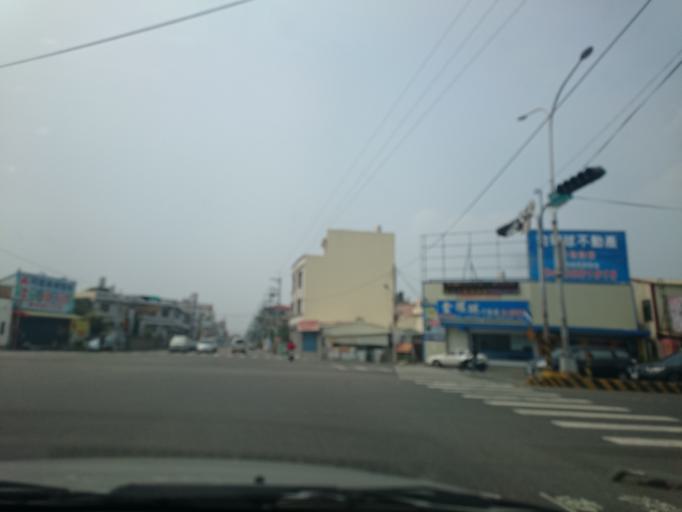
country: TW
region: Taiwan
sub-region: Nantou
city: Nantou
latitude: 23.8735
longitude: 120.5172
